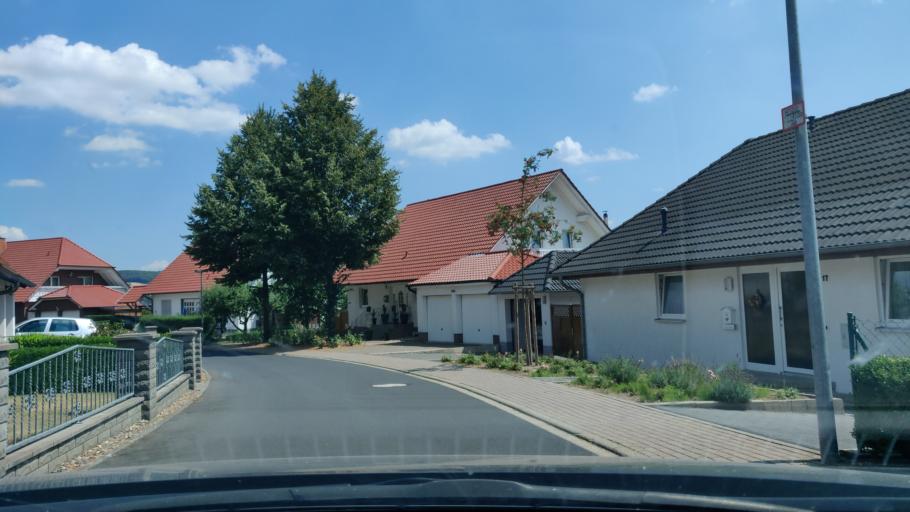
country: DE
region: Hesse
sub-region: Regierungsbezirk Kassel
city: Homberg
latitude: 51.0240
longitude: 9.4179
